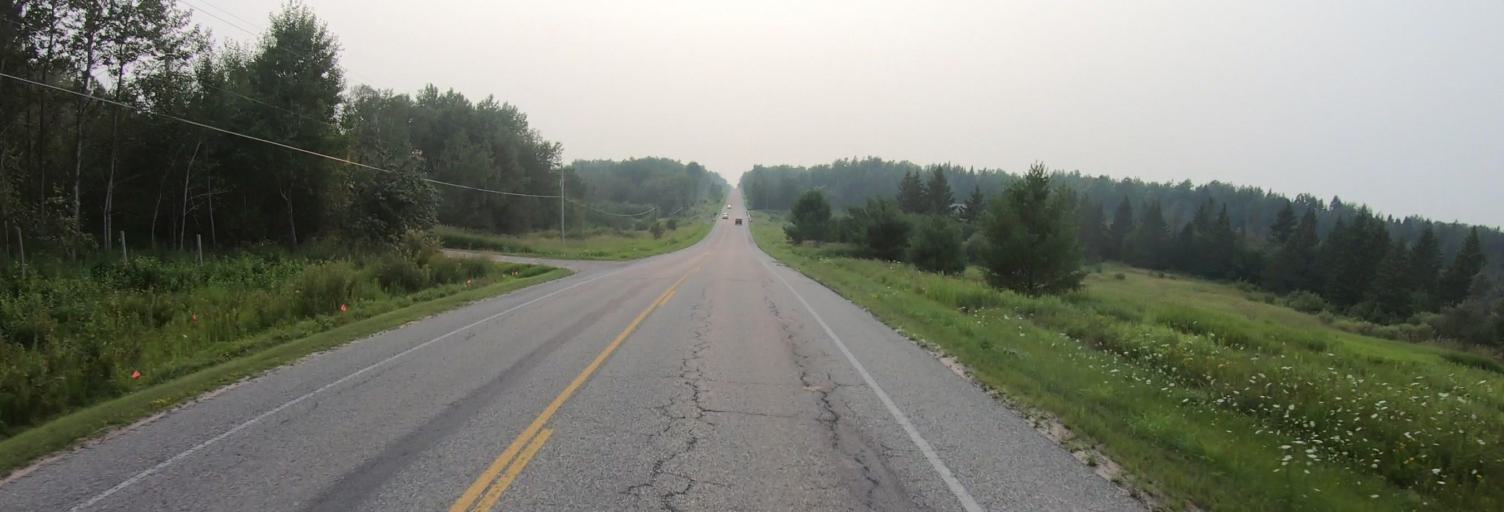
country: US
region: Michigan
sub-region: Chippewa County
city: Sault Ste. Marie
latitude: 46.4189
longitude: -84.4708
